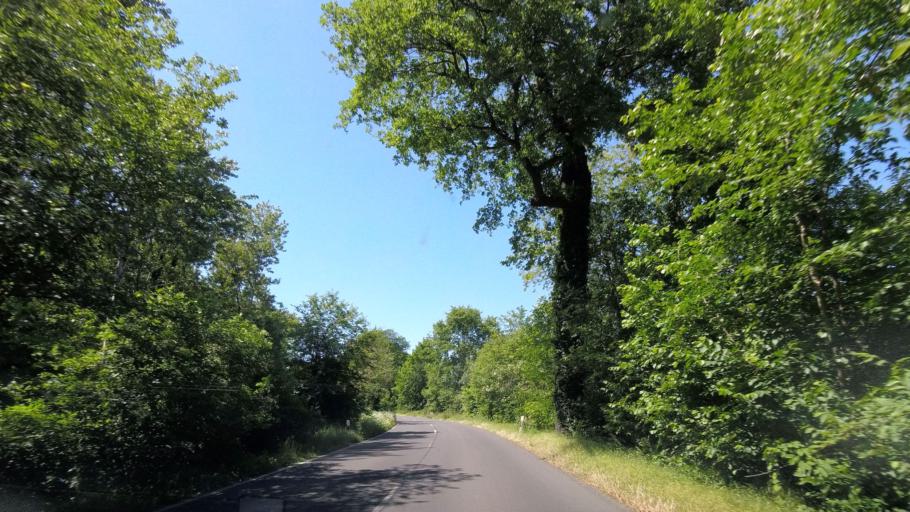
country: DE
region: Brandenburg
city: Potsdam
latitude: 52.3981
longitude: 13.0042
